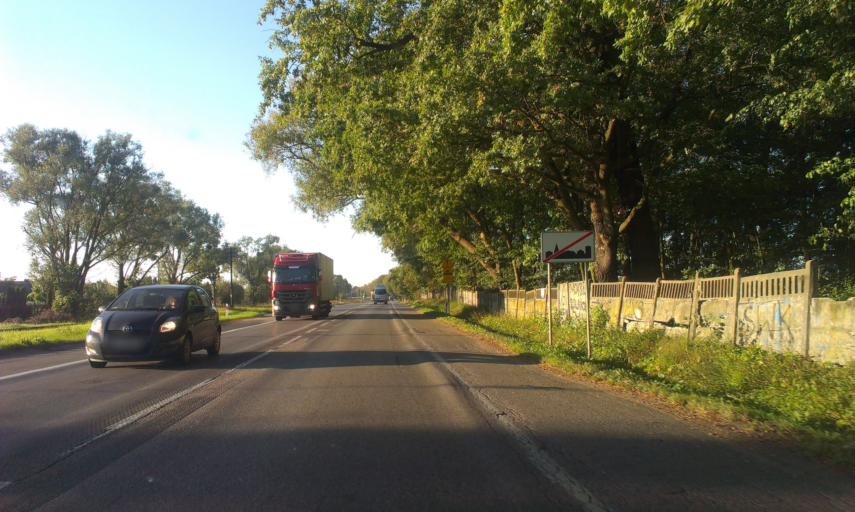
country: PL
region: Kujawsko-Pomorskie
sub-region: Powiat torunski
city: Lysomice
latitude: 53.0843
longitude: 18.6195
